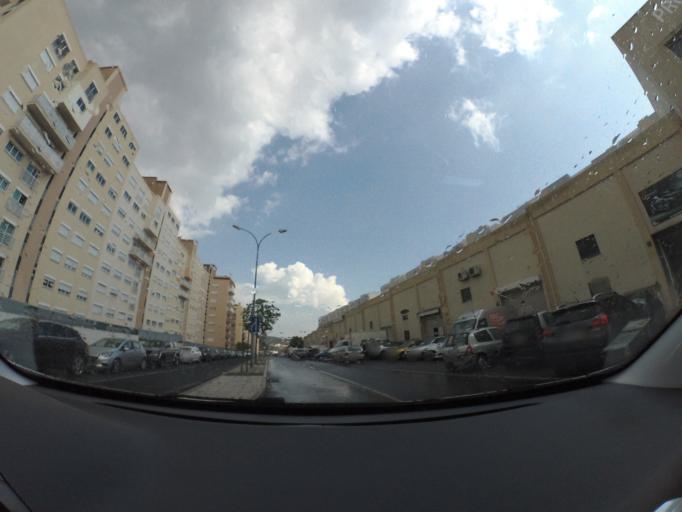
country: PT
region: Lisbon
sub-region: Oeiras
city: Linda-a-Velha
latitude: 38.7202
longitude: -9.2328
